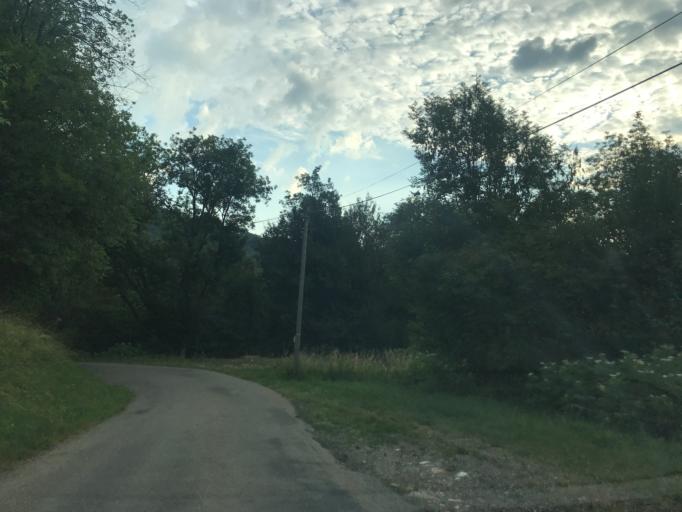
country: FR
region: Rhone-Alpes
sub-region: Departement de l'Isere
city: Saint-Vincent-de-Mercuze
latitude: 45.3891
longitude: 5.9339
